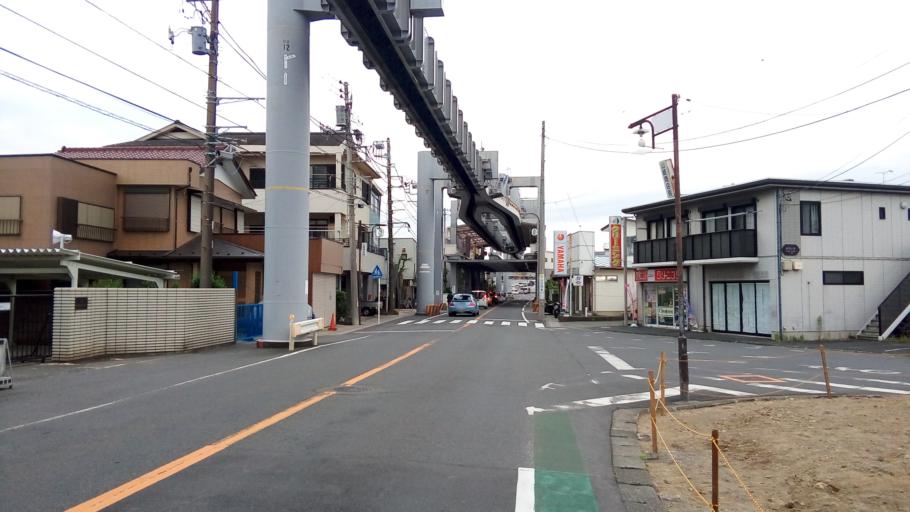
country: JP
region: Kanagawa
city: Kamakura
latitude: 35.3448
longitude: 139.5287
